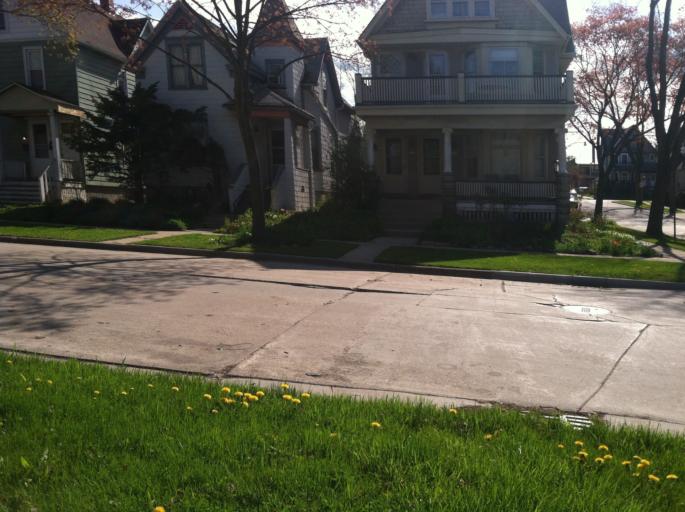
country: US
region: Wisconsin
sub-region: Milwaukee County
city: Shorewood
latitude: 43.0757
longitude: -87.8904
